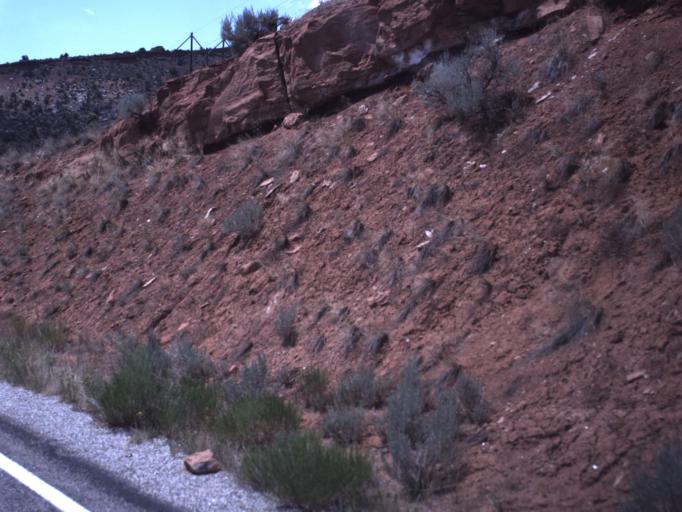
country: US
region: Utah
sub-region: Uintah County
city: Vernal
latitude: 40.5931
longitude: -109.4677
